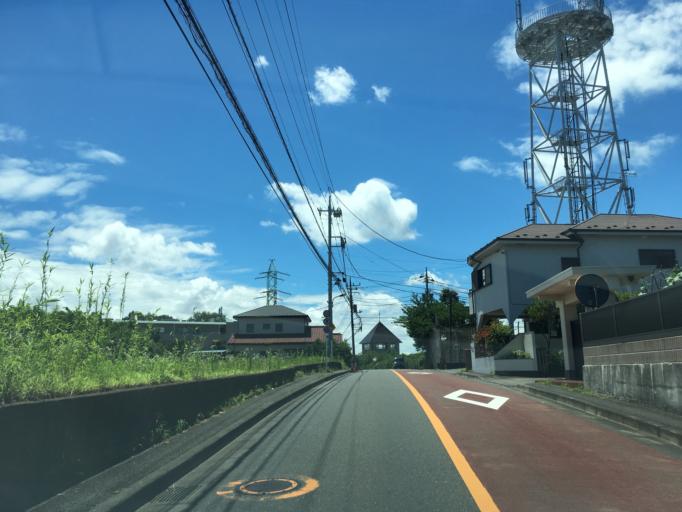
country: JP
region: Tokyo
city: Kokubunji
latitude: 35.6323
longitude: 139.4655
